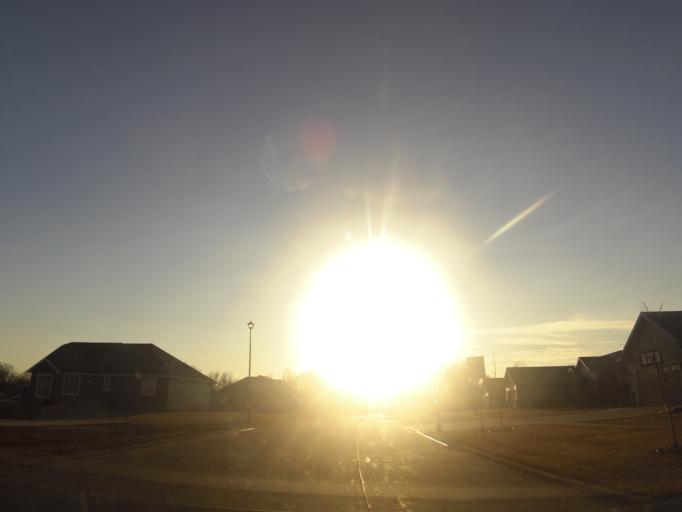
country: US
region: North Dakota
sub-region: Grand Forks County
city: Grand Forks
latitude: 47.8690
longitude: -97.0268
